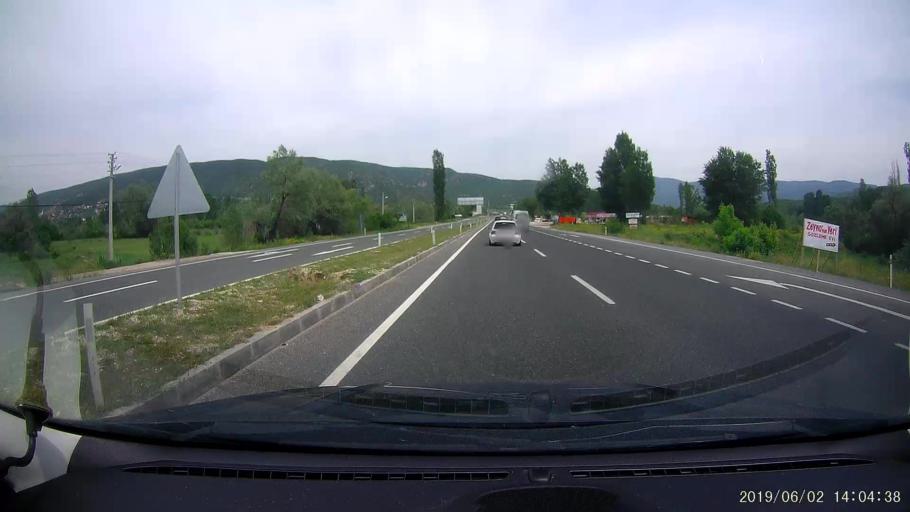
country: TR
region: Cankiri
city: Ilgaz
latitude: 40.9047
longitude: 33.6532
